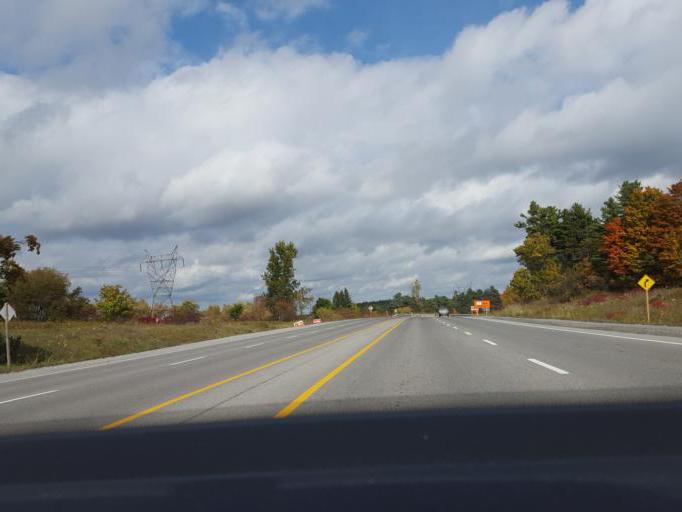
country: CA
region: Ontario
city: Pickering
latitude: 43.8840
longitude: -79.0969
